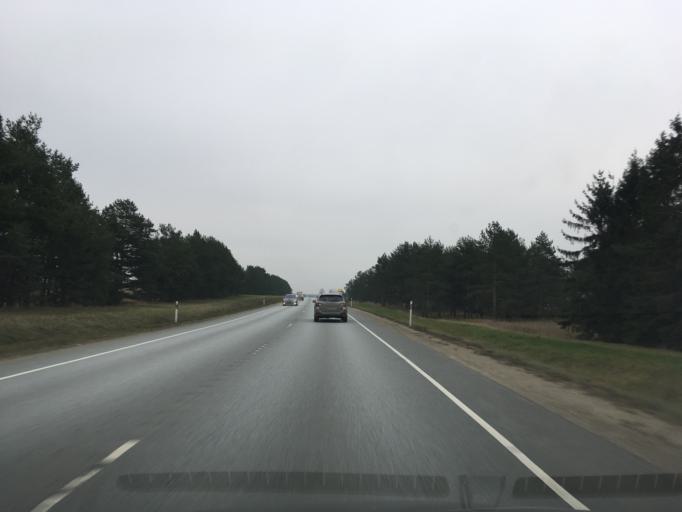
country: EE
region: Ida-Virumaa
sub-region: Puessi linn
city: Pussi
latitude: 59.4065
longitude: 27.0588
